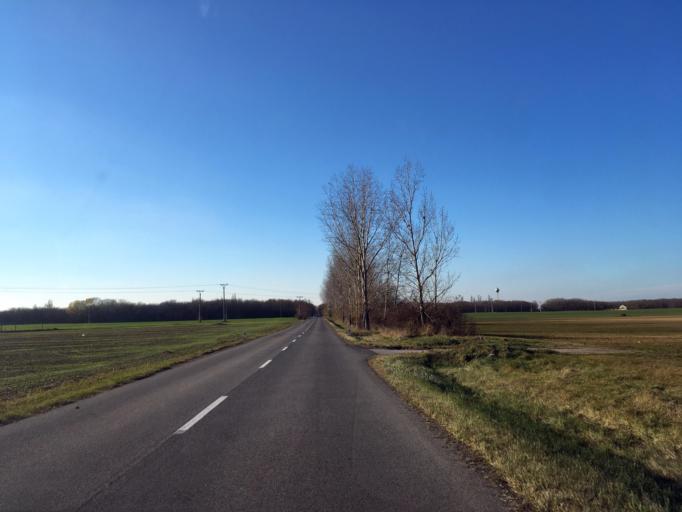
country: SK
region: Nitriansky
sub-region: Okres Komarno
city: Hurbanovo
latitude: 47.8967
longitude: 18.1740
